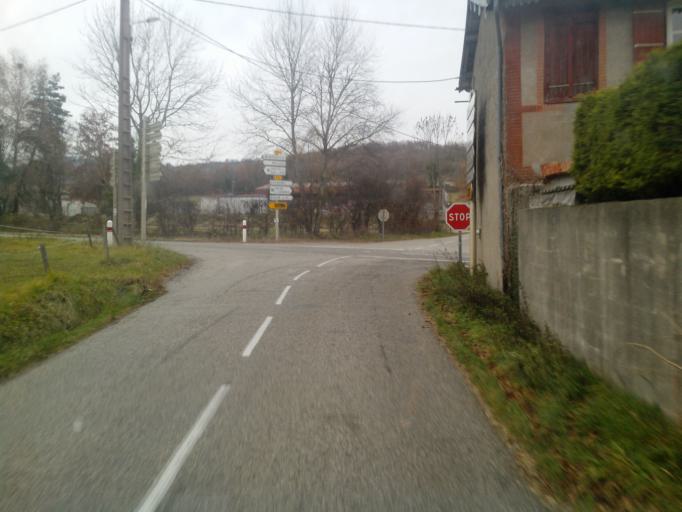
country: FR
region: Midi-Pyrenees
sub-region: Departement de l'Ariege
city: Varilhes
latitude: 43.0382
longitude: 1.5371
